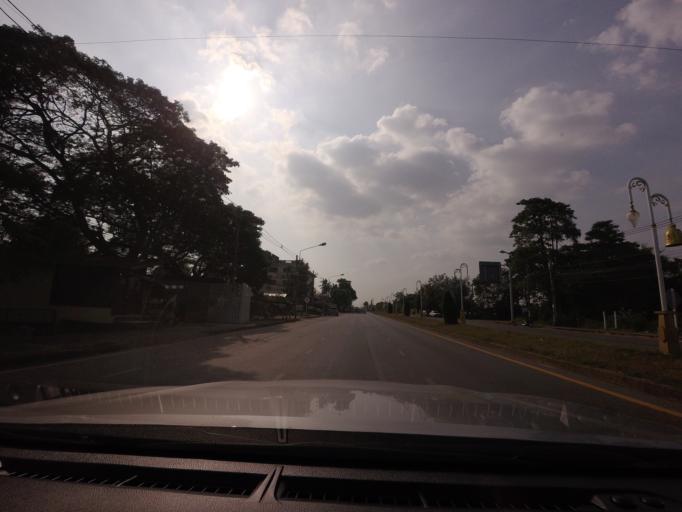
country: TH
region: Sukhothai
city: Sukhothai
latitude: 17.0108
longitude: 99.8348
